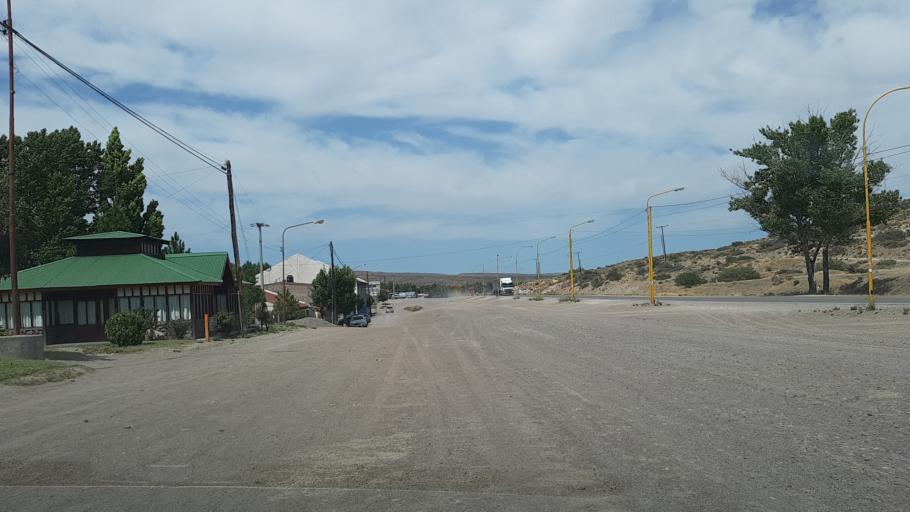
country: AR
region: Neuquen
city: Piedra del Aguila
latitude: -40.0442
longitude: -70.0719
